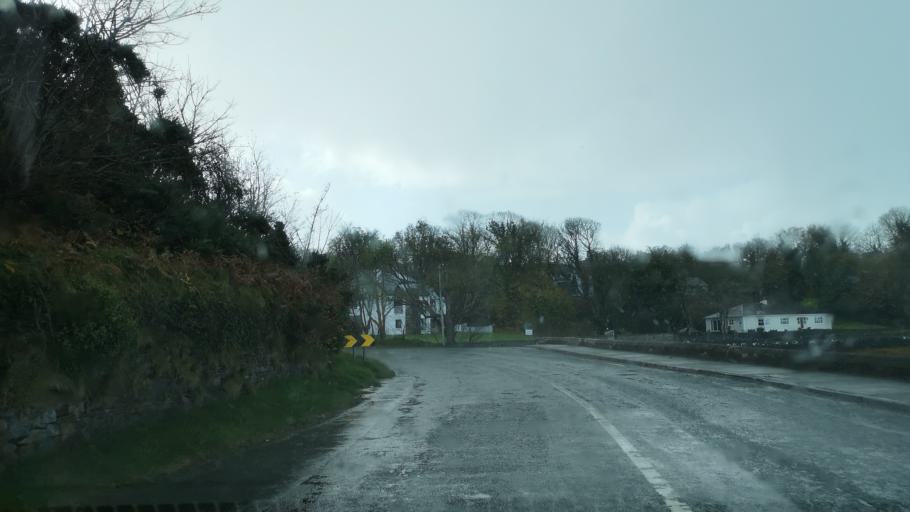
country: IE
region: Connaught
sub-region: Maigh Eo
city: Westport
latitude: 53.7920
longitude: -9.5678
